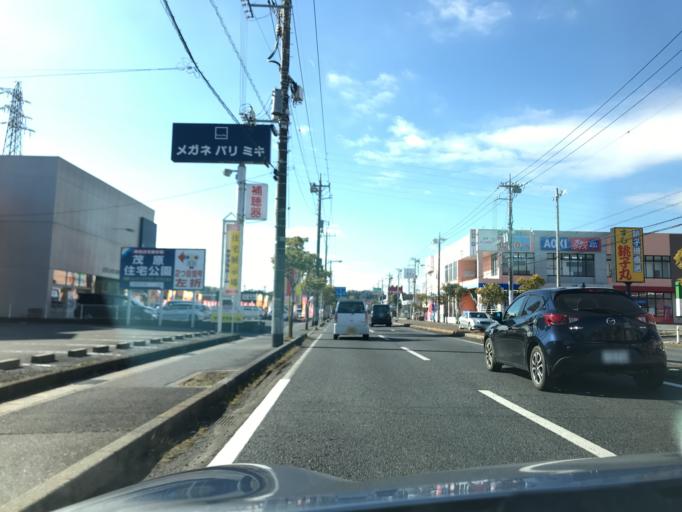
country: JP
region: Chiba
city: Mobara
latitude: 35.4397
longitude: 140.2895
